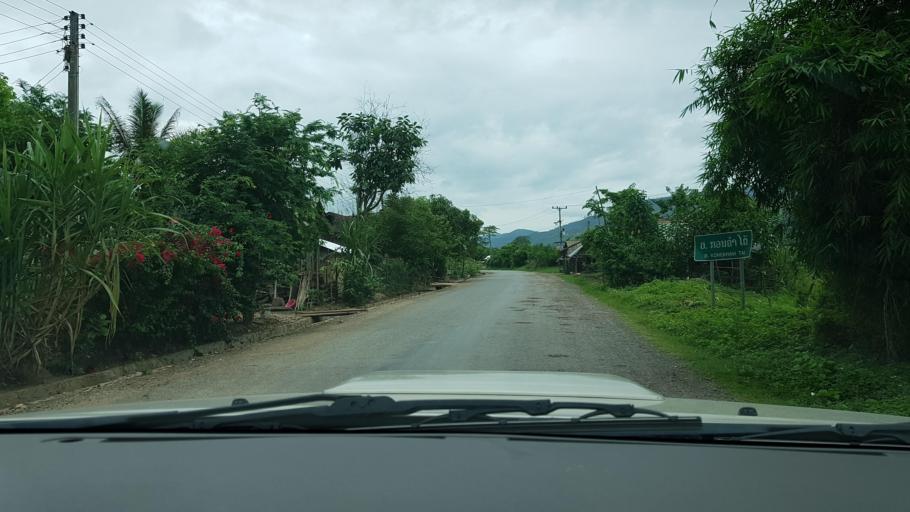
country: LA
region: Loungnamtha
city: Muang Nale
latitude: 20.2729
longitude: 101.6043
